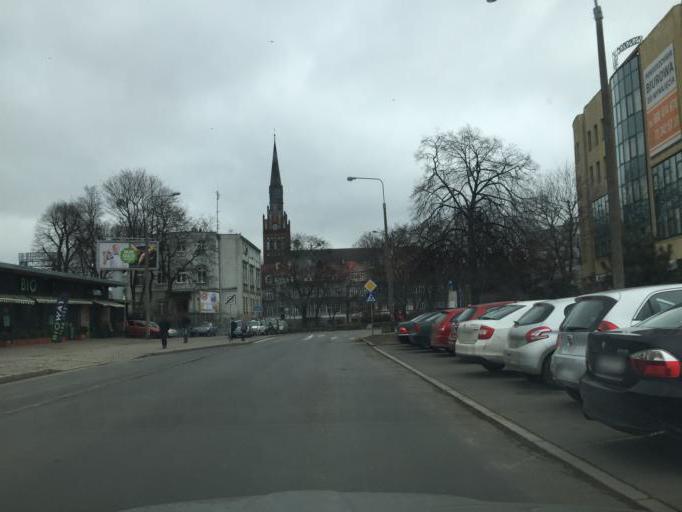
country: PL
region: Pomeranian Voivodeship
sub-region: Gdansk
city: Gdansk
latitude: 54.3808
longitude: 18.6065
